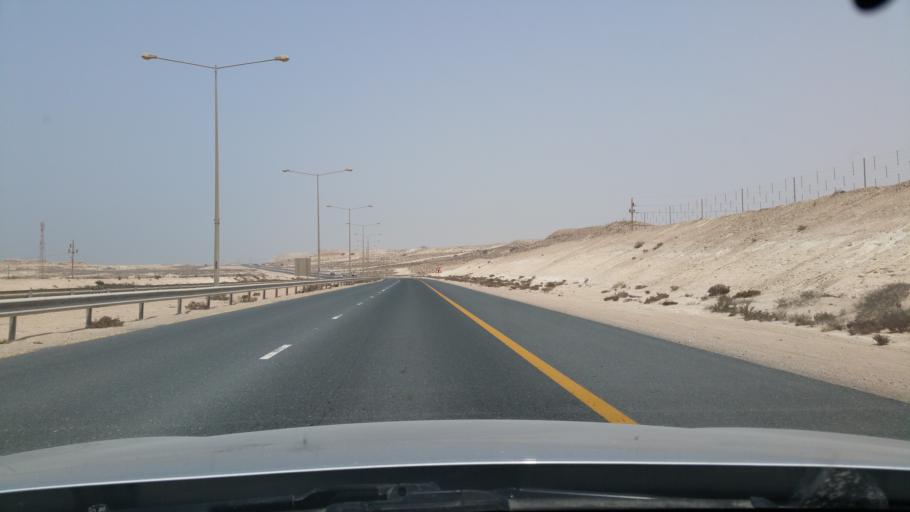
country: QA
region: Baladiyat ar Rayyan
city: Dukhan
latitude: 25.3425
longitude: 50.7832
